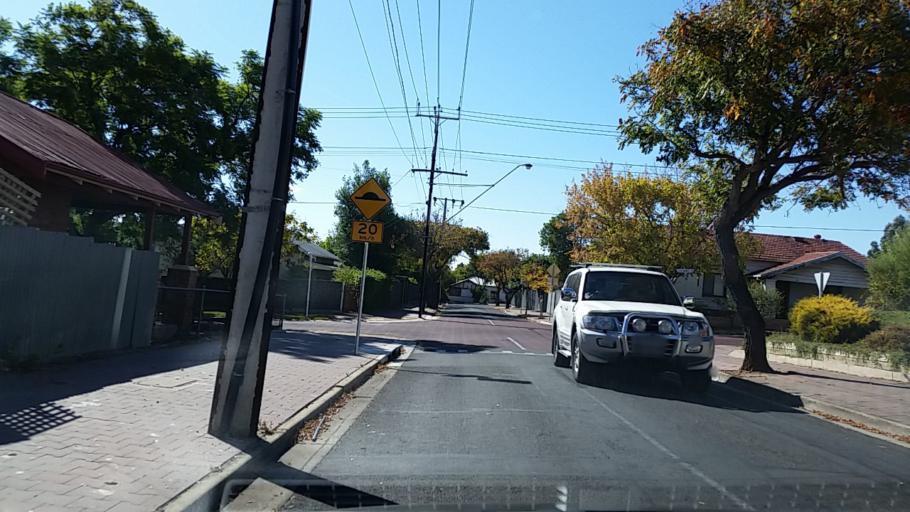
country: AU
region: South Australia
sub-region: Prospect
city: Prospect
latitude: -34.8826
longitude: 138.5892
